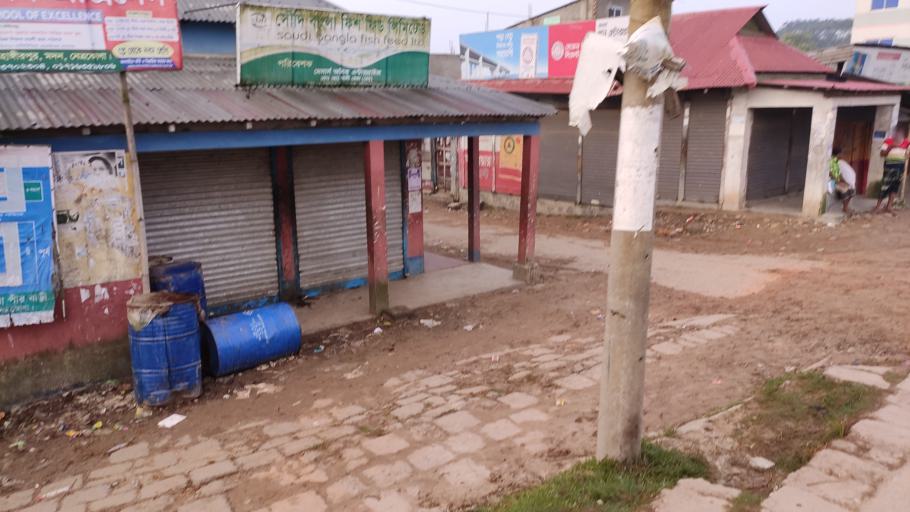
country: BD
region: Dhaka
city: Netrakona
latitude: 24.7167
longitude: 90.9512
